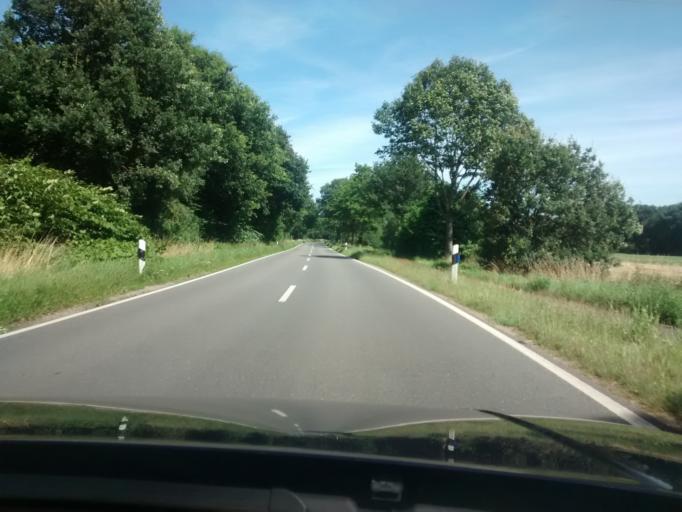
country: DE
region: Lower Saxony
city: Emlichheim
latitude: 52.6065
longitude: 6.8749
